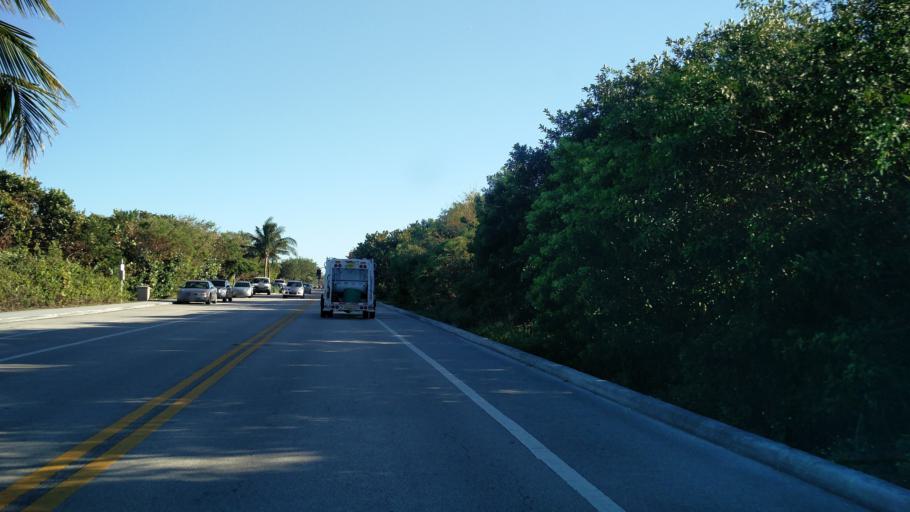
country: US
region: Florida
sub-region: Palm Beach County
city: Juno Beach
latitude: 26.9108
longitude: -80.0631
